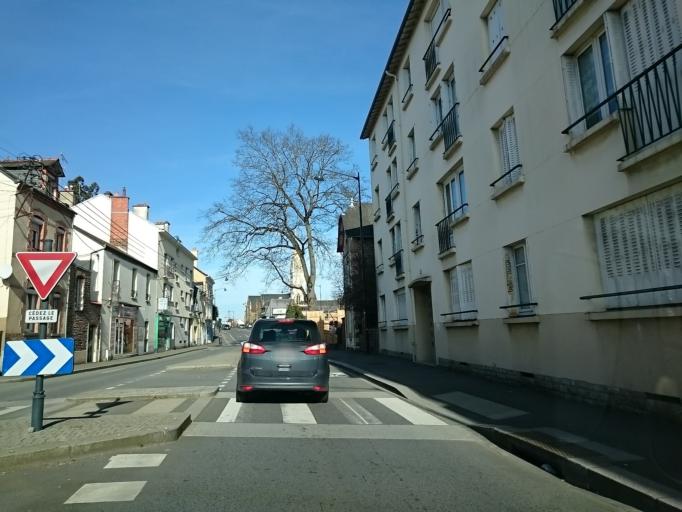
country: FR
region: Brittany
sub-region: Departement d'Ille-et-Vilaine
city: Rennes
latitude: 48.1014
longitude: -1.6594
